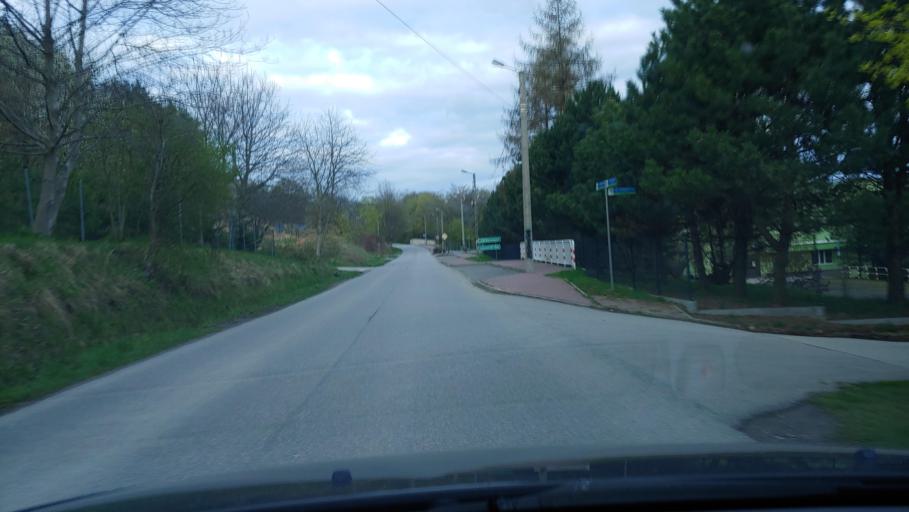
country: PL
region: Lesser Poland Voivodeship
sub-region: Powiat krakowski
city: Bolechowice
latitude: 50.1526
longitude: 19.7719
